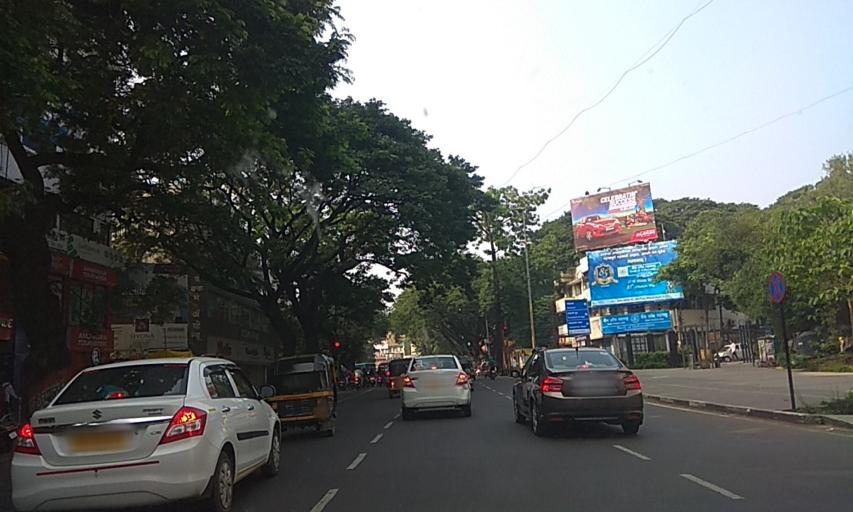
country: IN
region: Maharashtra
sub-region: Pune Division
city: Pune
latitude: 18.5175
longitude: 73.8437
